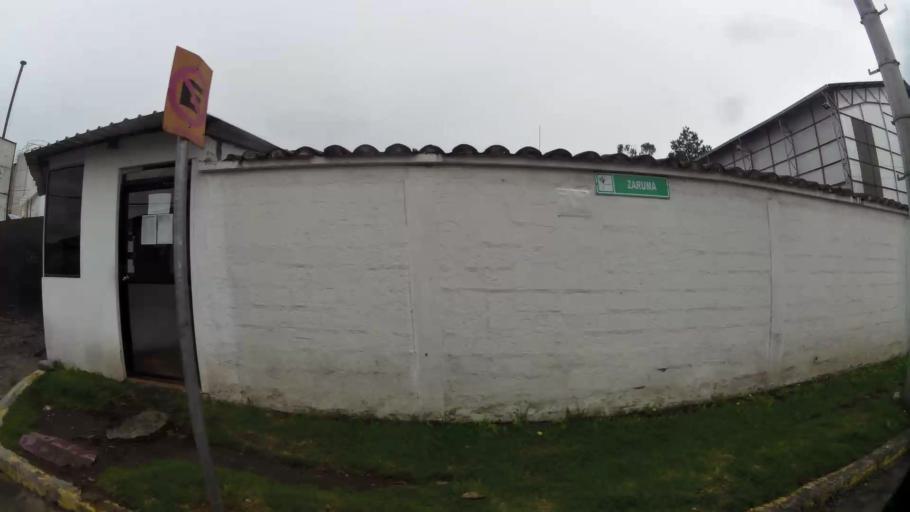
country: EC
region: Pichincha
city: Sangolqui
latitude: -0.3222
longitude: -78.4381
